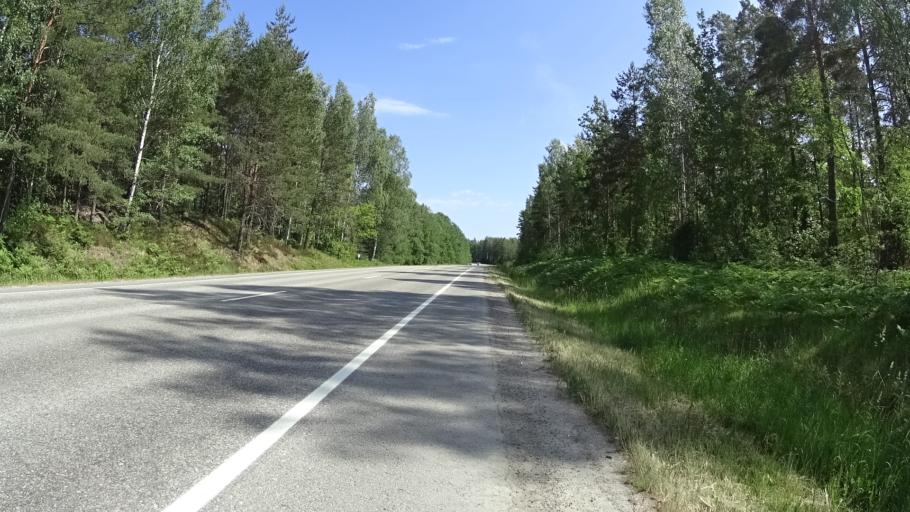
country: FI
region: Uusimaa
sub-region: Raaseporin
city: Karis
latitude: 60.0907
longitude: 23.6422
